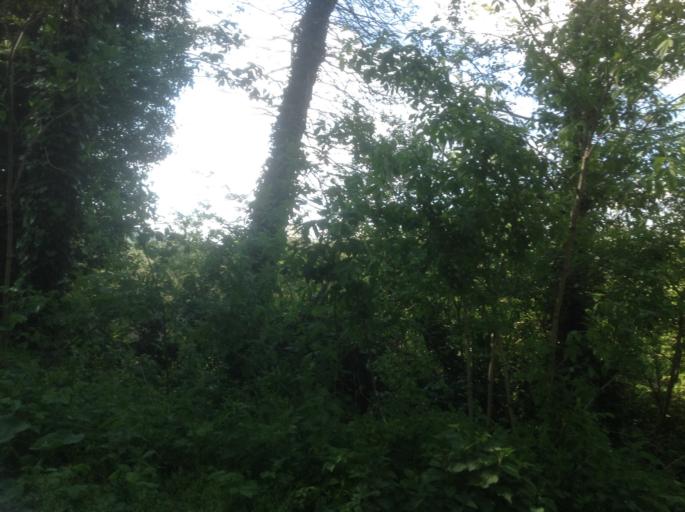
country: IT
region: Latium
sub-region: Provincia di Rieti
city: Colli sul Velino
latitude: 42.4775
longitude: 12.8078
